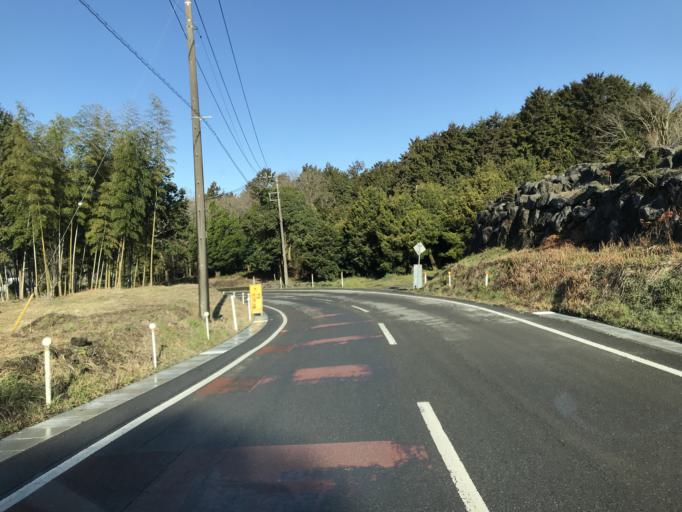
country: JP
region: Shizuoka
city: Fujinomiya
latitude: 35.2390
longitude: 138.6682
